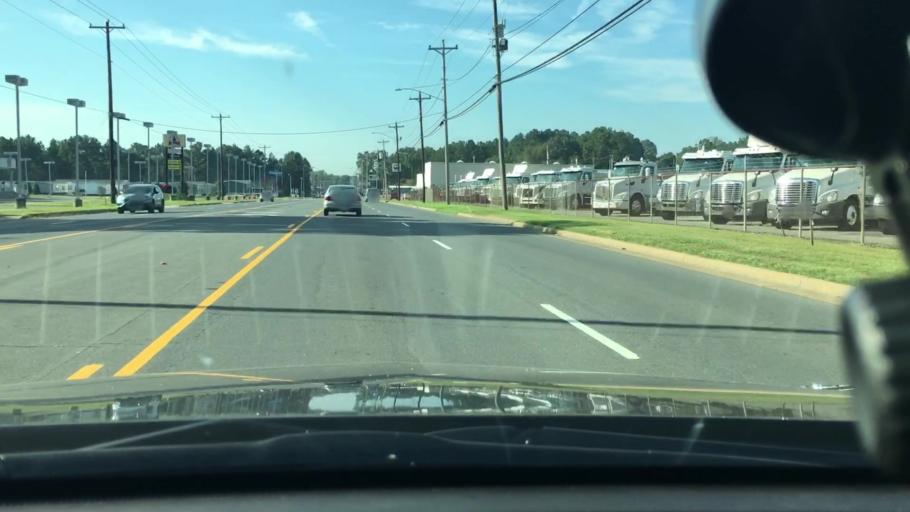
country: US
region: North Carolina
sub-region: Stanly County
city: Albemarle
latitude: 35.3789
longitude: -80.1948
